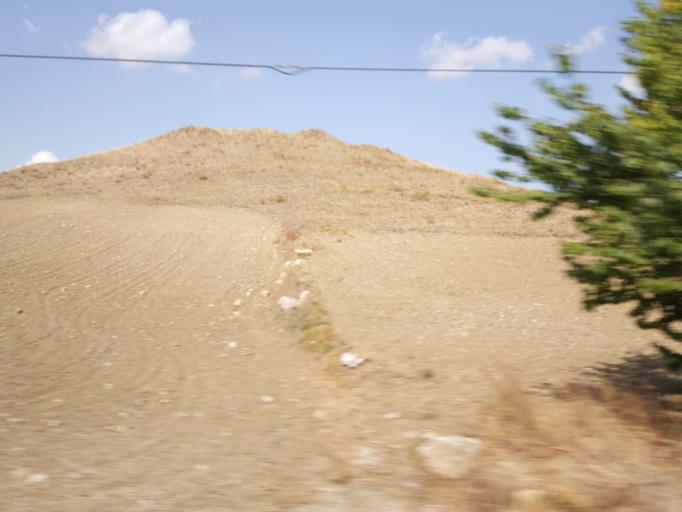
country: TR
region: Corum
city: Bogazkale
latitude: 40.1414
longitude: 34.5709
